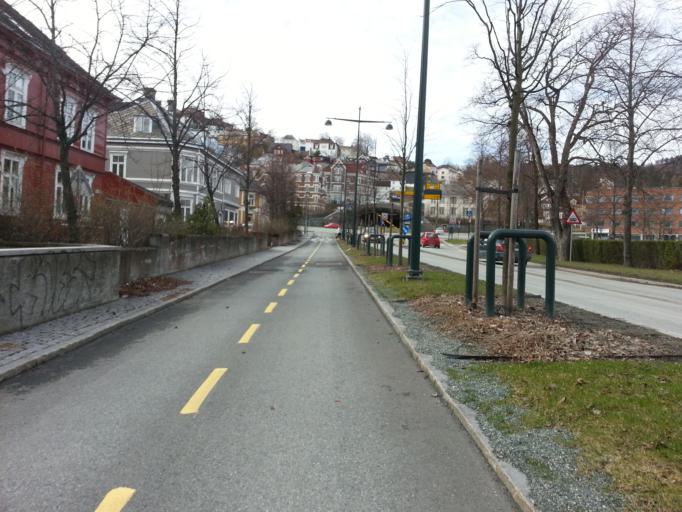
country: NO
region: Sor-Trondelag
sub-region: Trondheim
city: Trondheim
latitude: 63.4286
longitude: 10.3693
